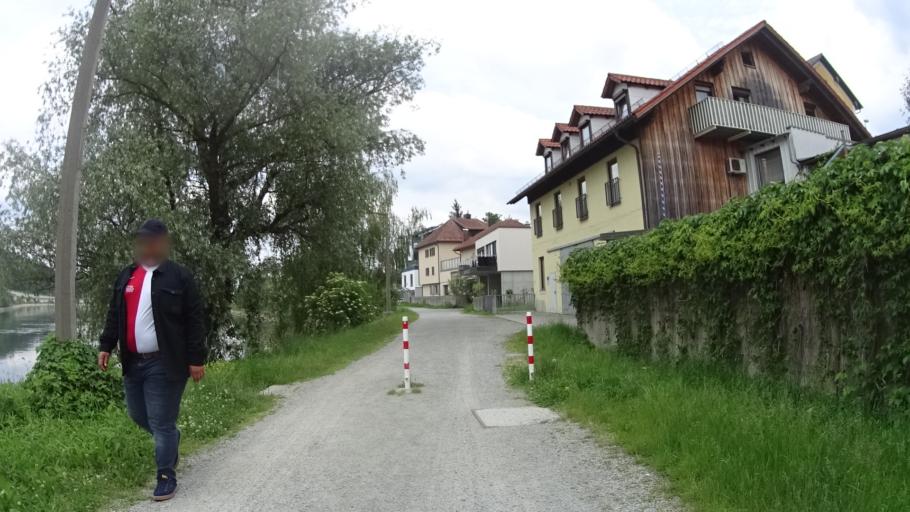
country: DE
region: Bavaria
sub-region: Lower Bavaria
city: Passau
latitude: 48.5740
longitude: 13.4197
